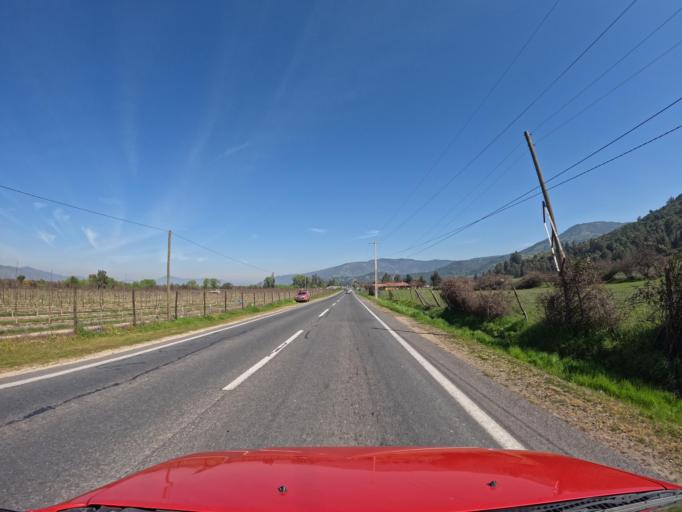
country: CL
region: Maule
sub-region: Provincia de Curico
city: Rauco
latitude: -34.9783
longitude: -71.3946
